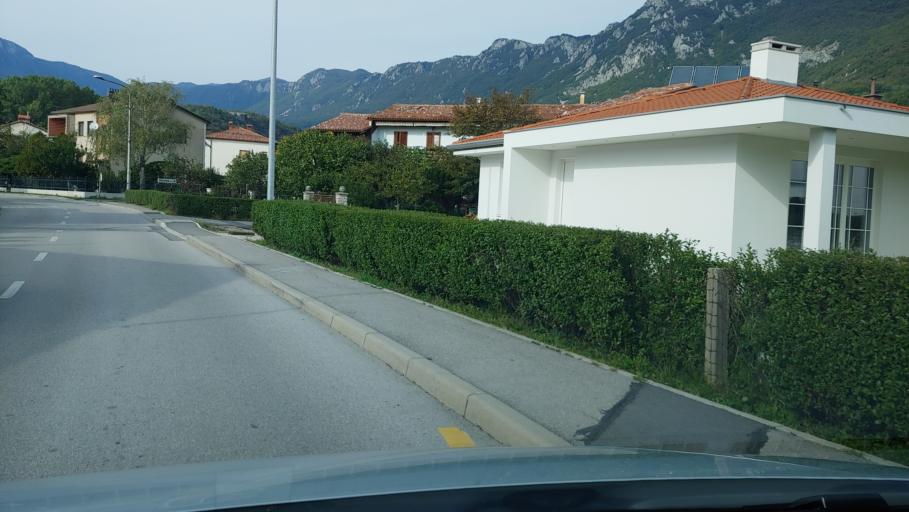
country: SI
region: Ajdovscina
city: Ajdovscina
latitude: 45.8890
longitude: 13.9083
